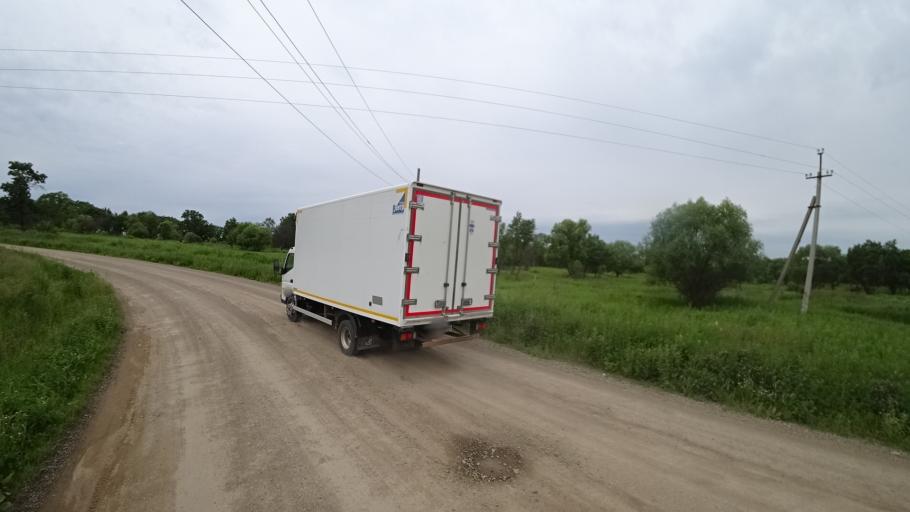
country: RU
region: Primorskiy
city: Novosysoyevka
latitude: 44.2025
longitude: 133.3155
